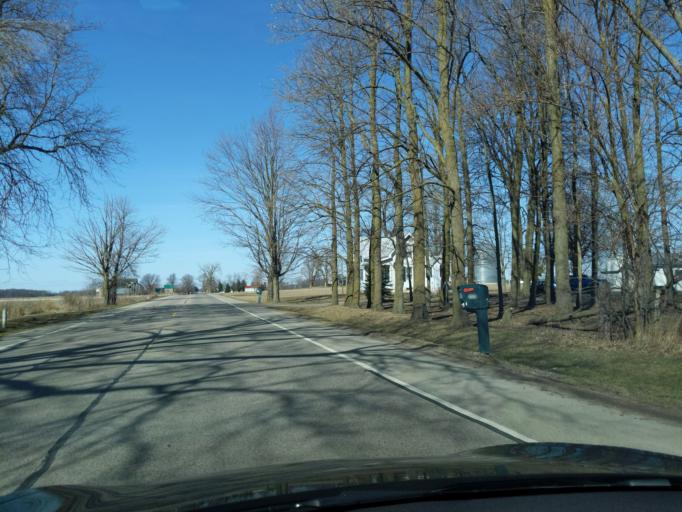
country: US
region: Michigan
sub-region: Ionia County
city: Lake Odessa
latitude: 42.8078
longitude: -85.1336
